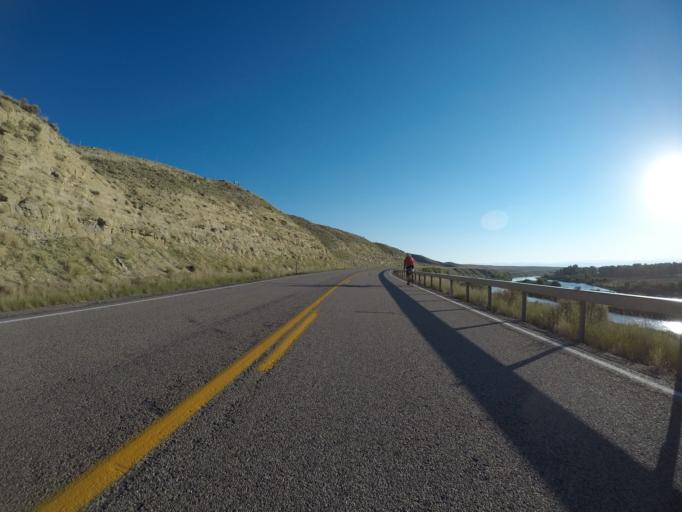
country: US
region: Wyoming
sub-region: Sublette County
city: Marbleton
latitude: 42.5823
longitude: -109.9232
